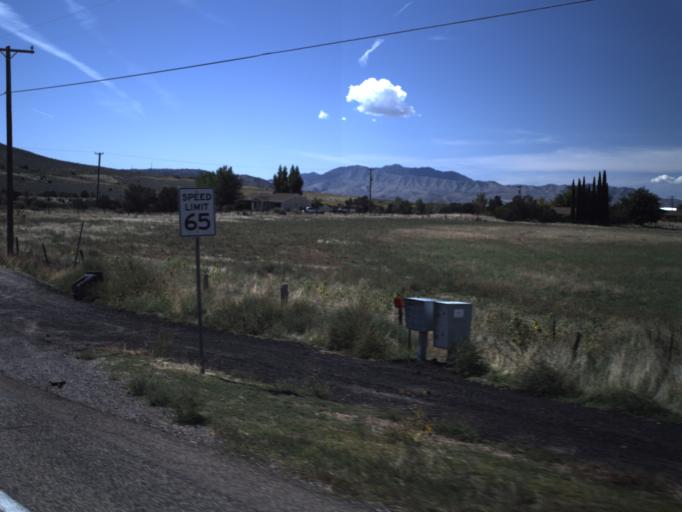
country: US
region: Utah
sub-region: Washington County
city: Ivins
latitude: 37.3343
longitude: -113.6932
